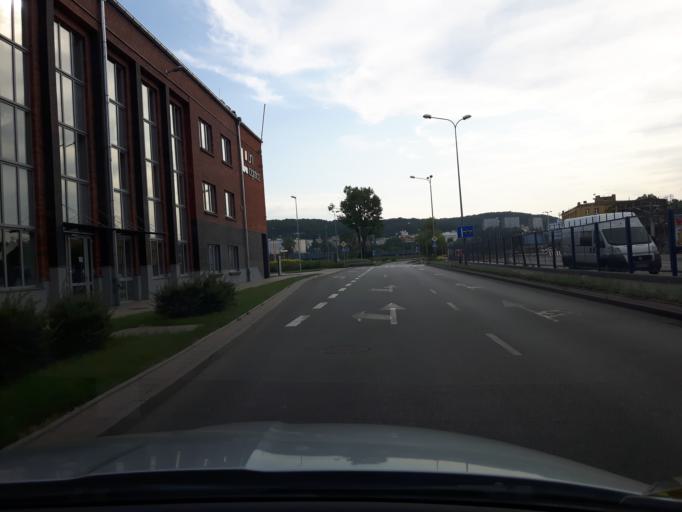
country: PL
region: Pomeranian Voivodeship
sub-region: Gdynia
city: Gdynia
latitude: 54.5278
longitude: 18.5315
